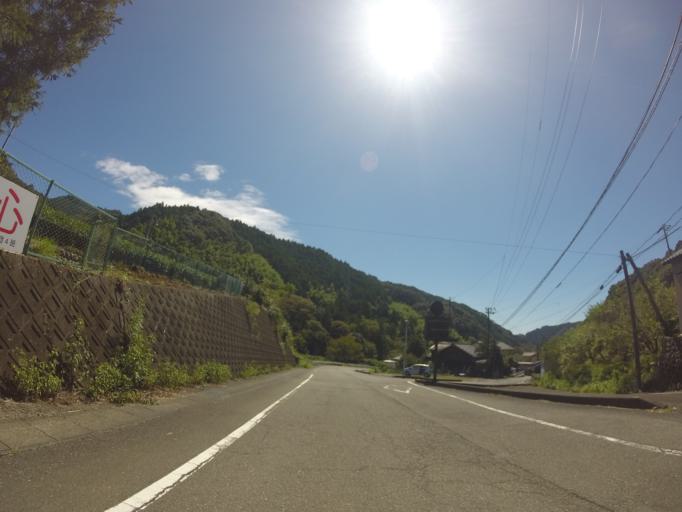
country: JP
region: Shizuoka
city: Fujieda
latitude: 34.9669
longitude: 138.2127
